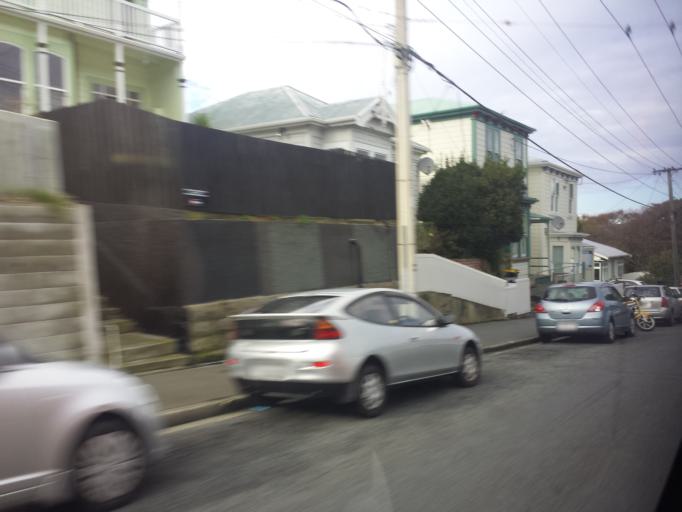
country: NZ
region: Wellington
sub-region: Wellington City
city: Wellington
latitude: -41.3062
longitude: 174.7934
